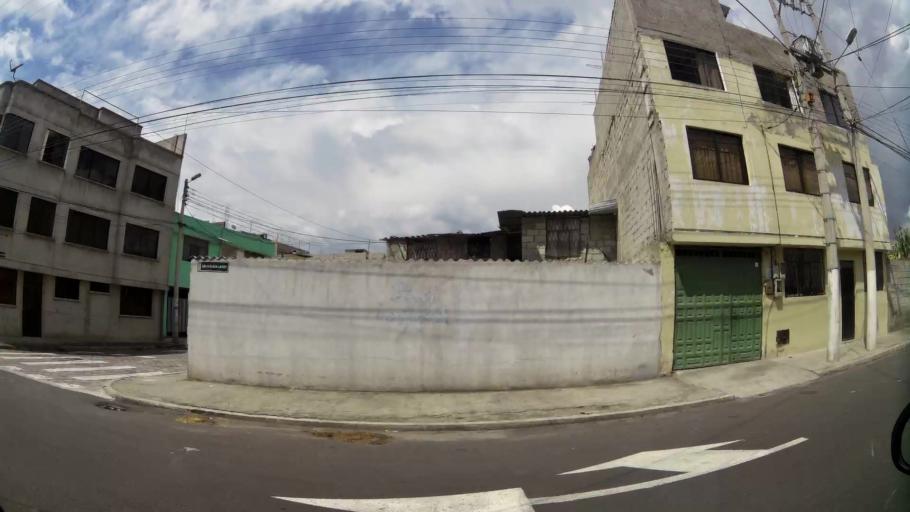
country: EC
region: Pichincha
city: Quito
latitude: -0.0977
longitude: -78.4547
